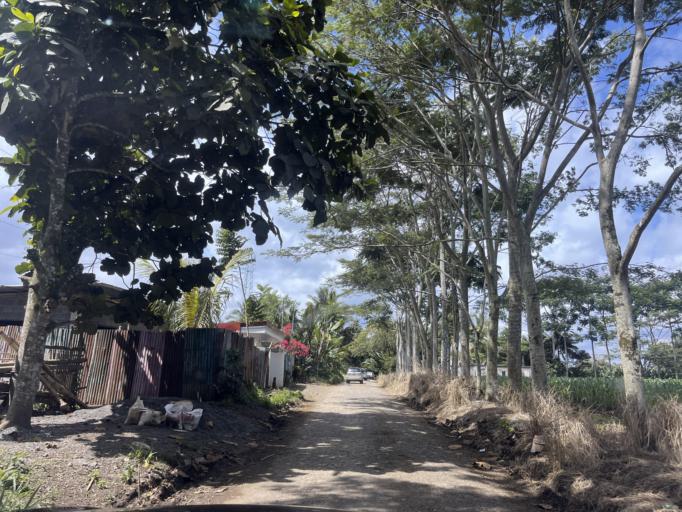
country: PH
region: Northern Mindanao
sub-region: Province of Bukidnon
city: Impalutao
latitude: 8.2722
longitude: 125.0188
